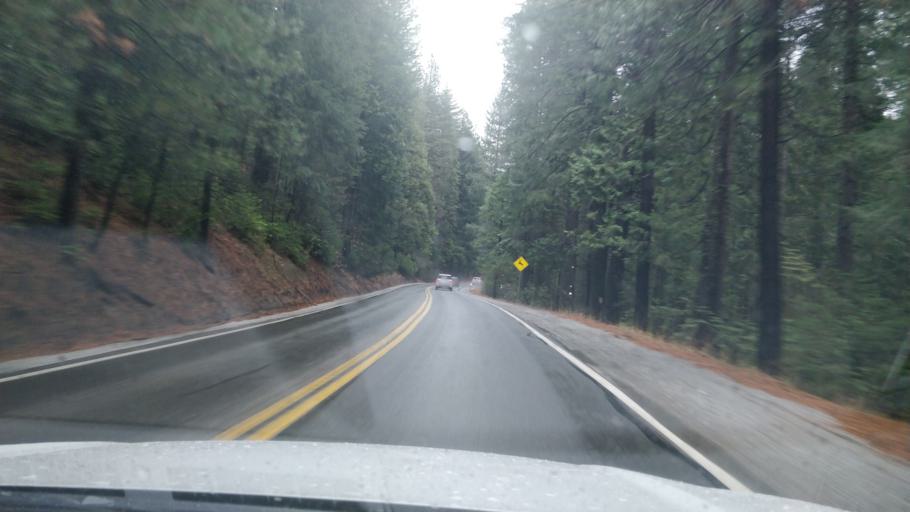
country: US
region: California
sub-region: Nevada County
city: Nevada City
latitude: 39.3156
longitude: -120.8021
